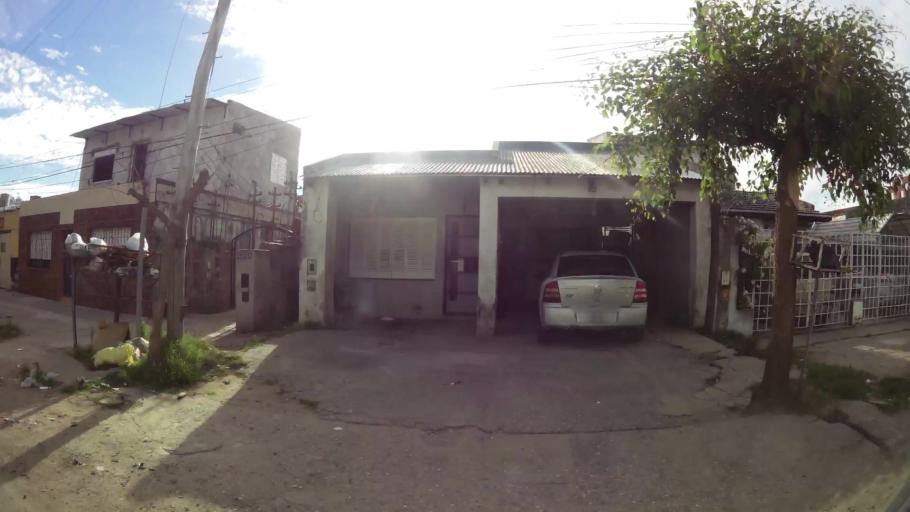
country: AR
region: Santa Fe
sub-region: Departamento de Rosario
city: Rosario
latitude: -32.9747
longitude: -60.6868
